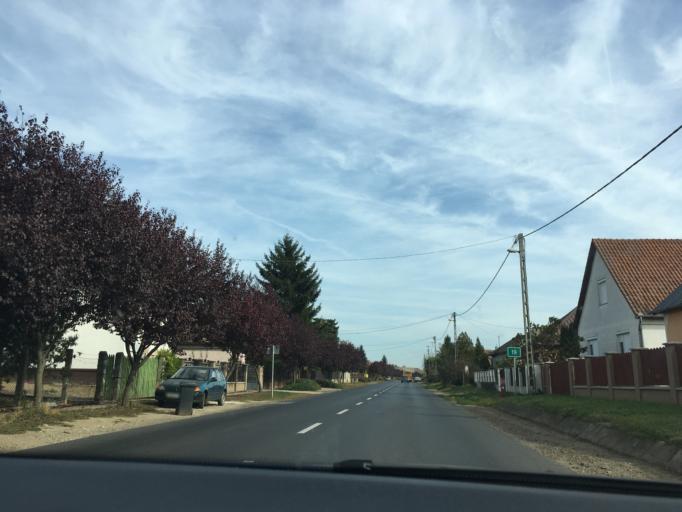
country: HU
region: Szabolcs-Szatmar-Bereg
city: Kallosemjen
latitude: 47.8599
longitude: 21.9089
